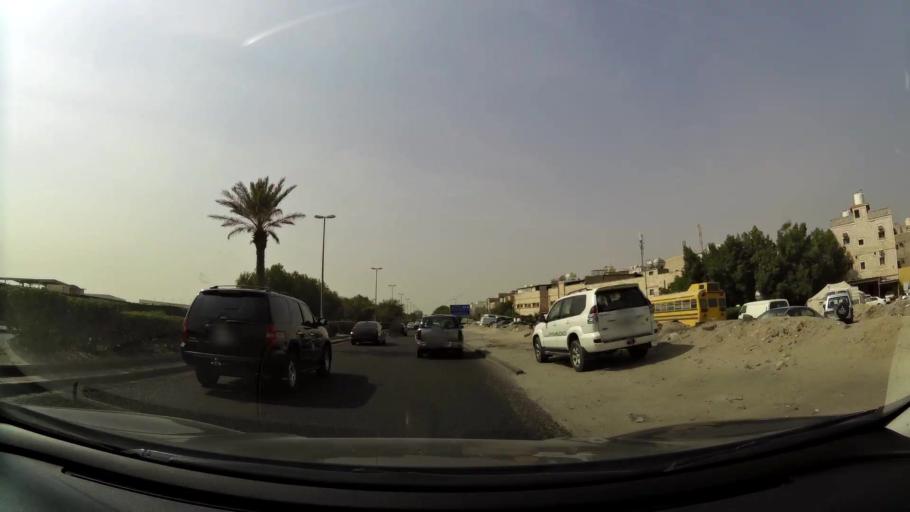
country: KW
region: Al Farwaniyah
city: Al Farwaniyah
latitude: 29.2507
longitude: 47.9446
